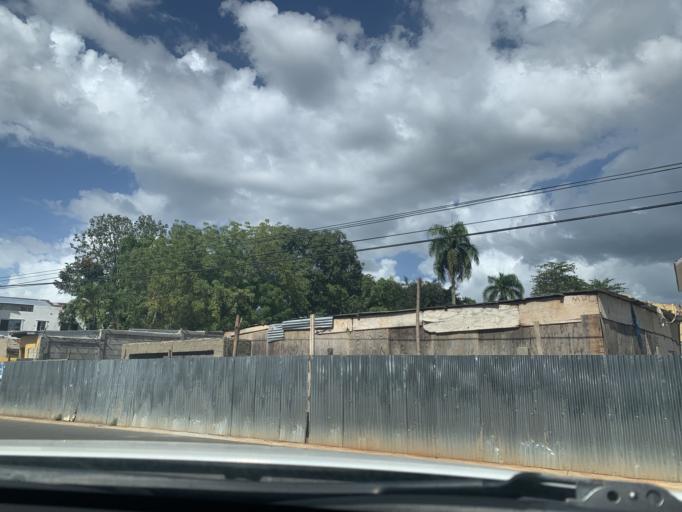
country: DO
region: Monte Plata
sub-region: Yamasa
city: Yamasa
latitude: 18.7678
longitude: -70.0241
